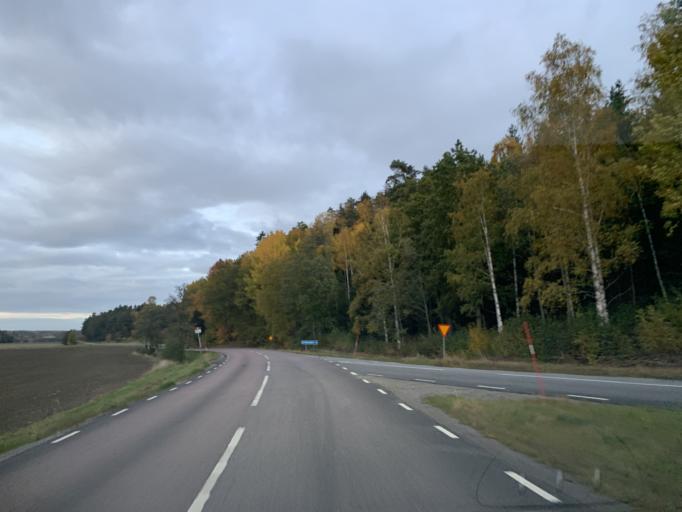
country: SE
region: Stockholm
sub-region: Nynashamns Kommun
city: Osmo
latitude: 58.9715
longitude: 17.7759
